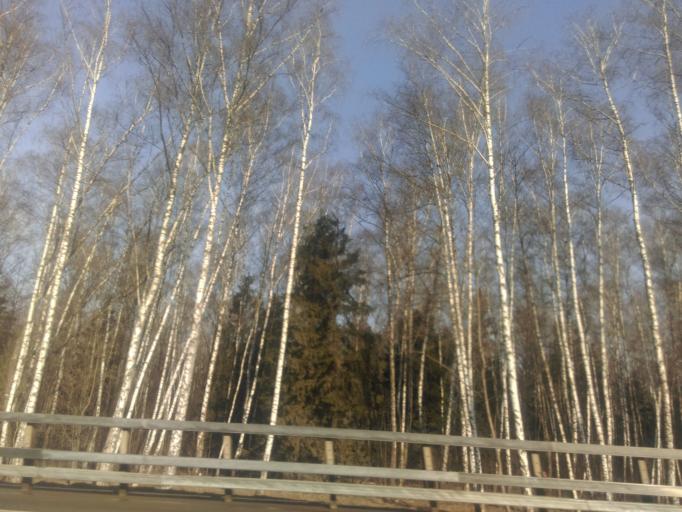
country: RU
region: Moscow
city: Novo-Peredelkino
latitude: 55.6299
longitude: 37.3159
